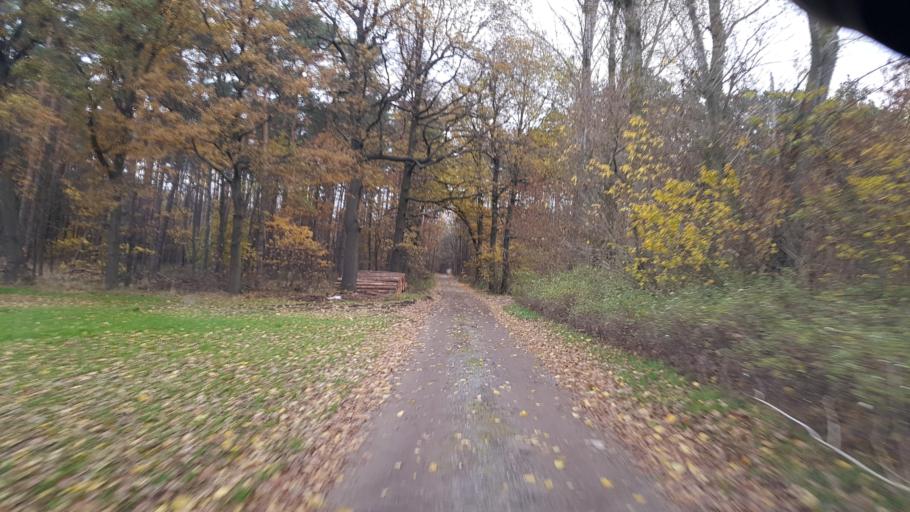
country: DE
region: Brandenburg
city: Sallgast
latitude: 51.6156
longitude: 13.8763
